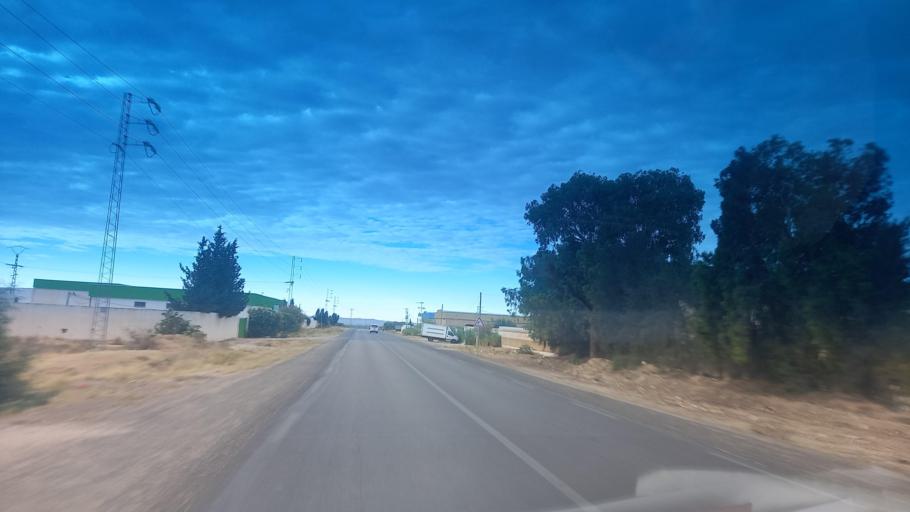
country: TN
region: Al Qasrayn
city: Sbiba
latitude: 35.2853
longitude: 9.0931
